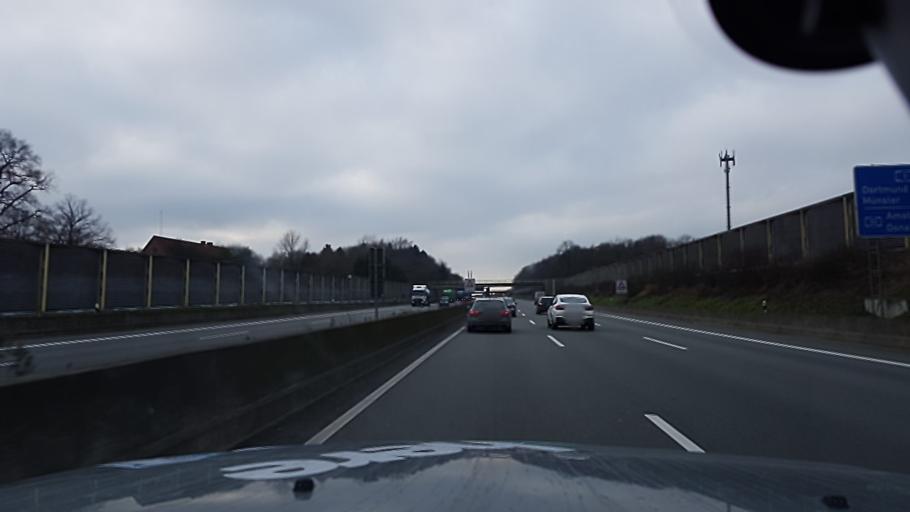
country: DE
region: Lower Saxony
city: Wallenhorst
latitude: 52.3356
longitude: 8.0050
